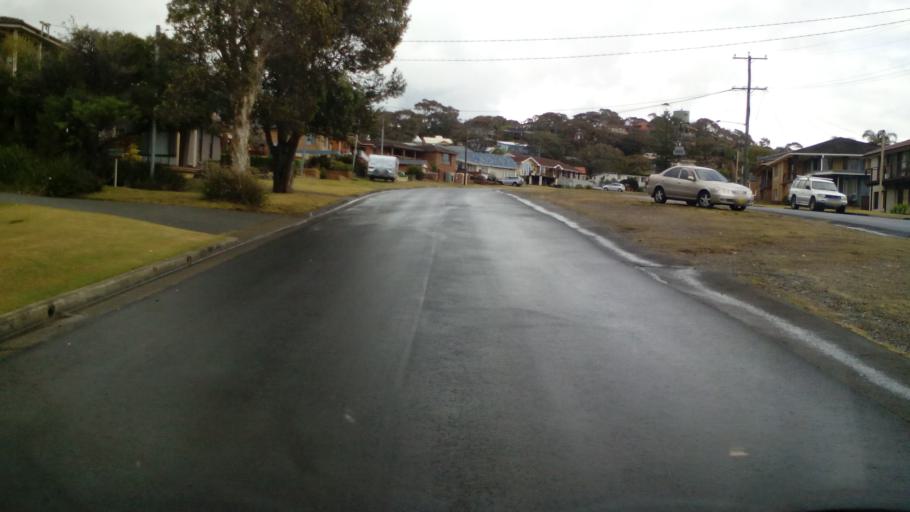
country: AU
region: New South Wales
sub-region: Lake Macquarie Shire
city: Belmont South
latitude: -33.1102
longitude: 151.6446
